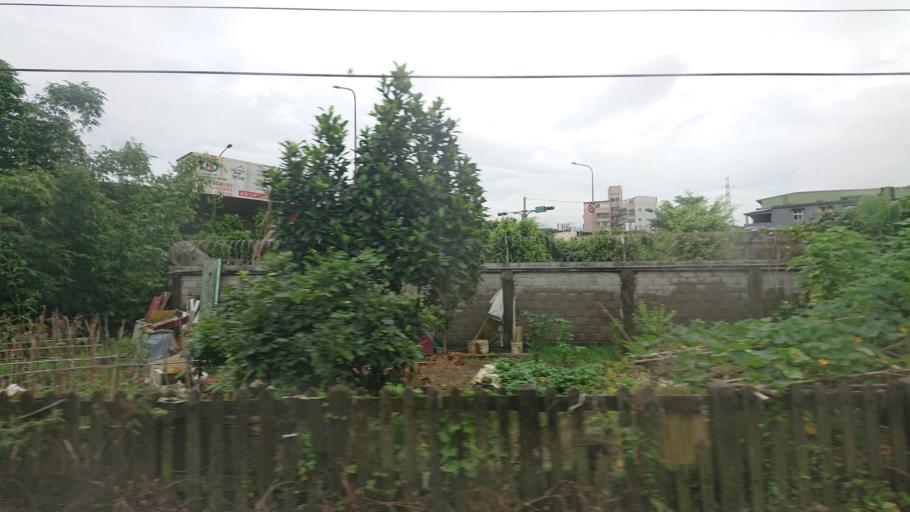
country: TW
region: Taiwan
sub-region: Keelung
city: Keelung
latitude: 25.0783
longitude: 121.6898
